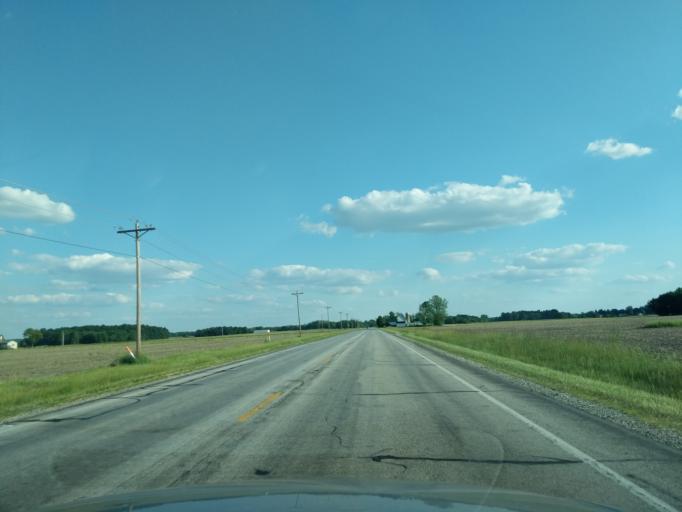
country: US
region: Indiana
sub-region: Whitley County
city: Tri-Lakes
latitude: 41.2983
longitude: -85.5005
